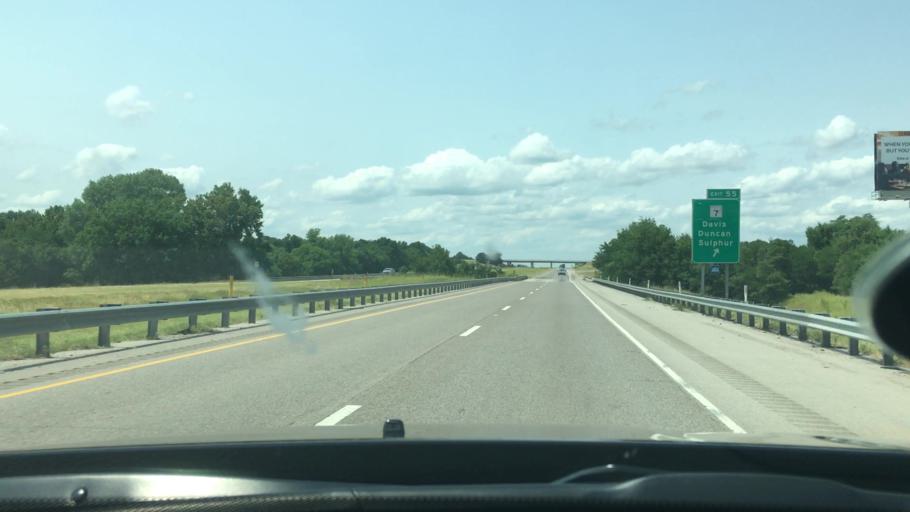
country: US
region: Oklahoma
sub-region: Murray County
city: Davis
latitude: 34.4996
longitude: -97.1694
